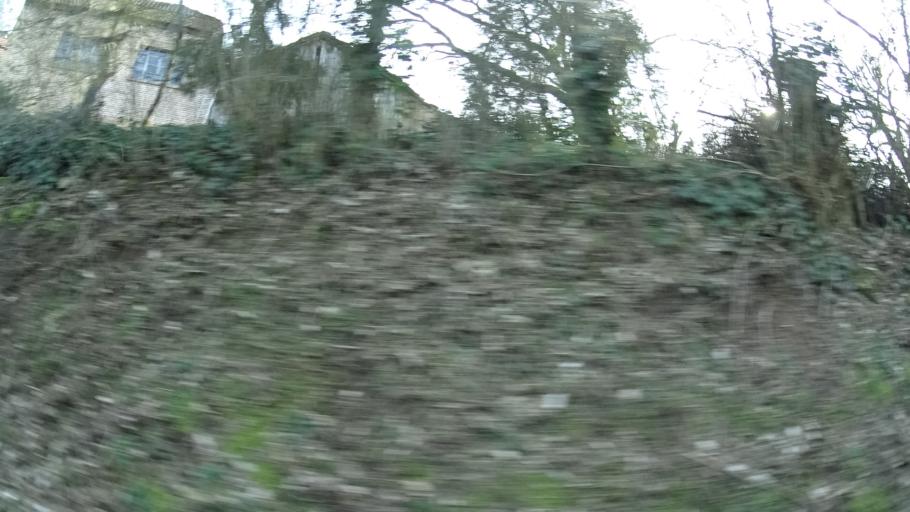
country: DE
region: Rheinland-Pfalz
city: Oberstaufenbach
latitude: 49.5046
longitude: 7.5251
